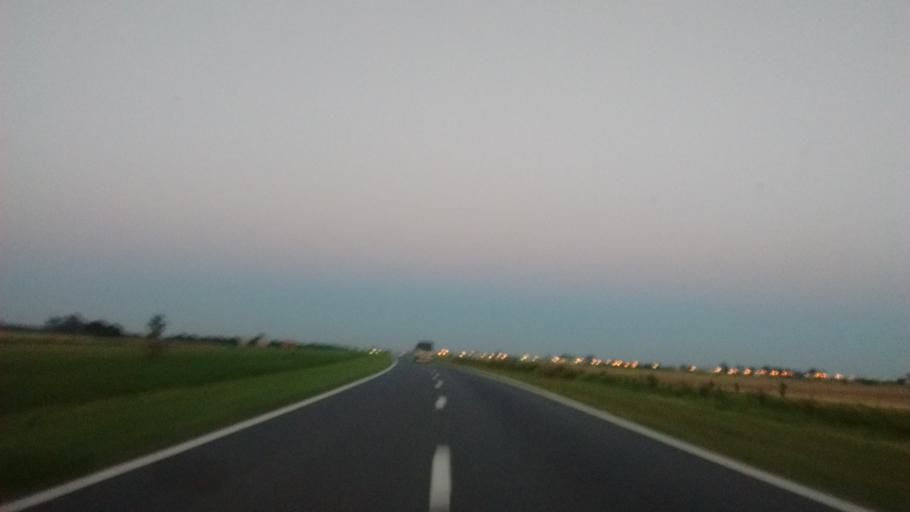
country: AR
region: Santa Fe
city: Roldan
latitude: -32.9205
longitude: -60.9220
